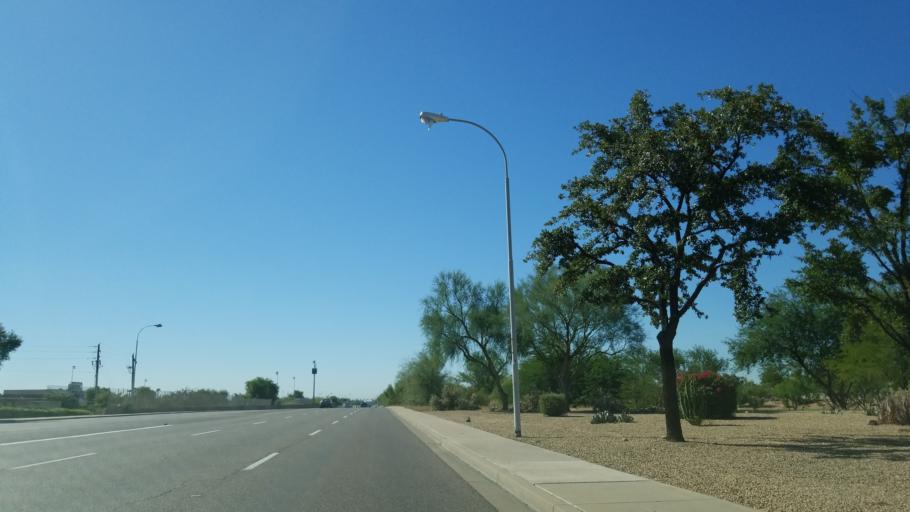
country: US
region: Arizona
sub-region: Maricopa County
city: Scottsdale
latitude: 33.5346
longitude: -111.9088
